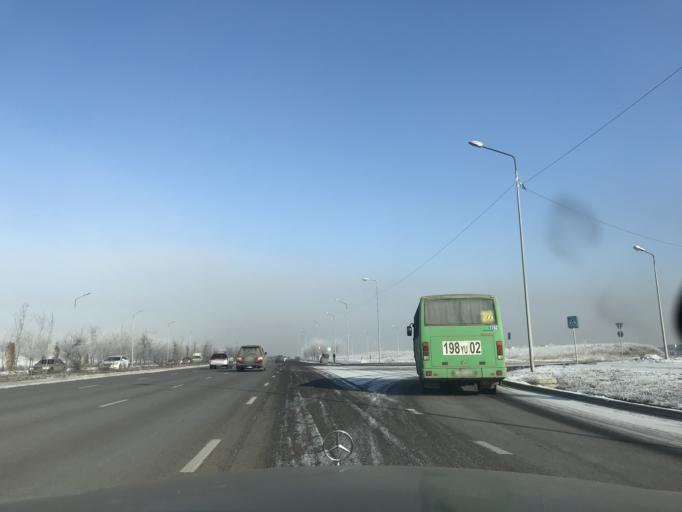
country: KZ
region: Almaty Oblysy
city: Burunday
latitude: 43.3003
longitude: 76.8351
